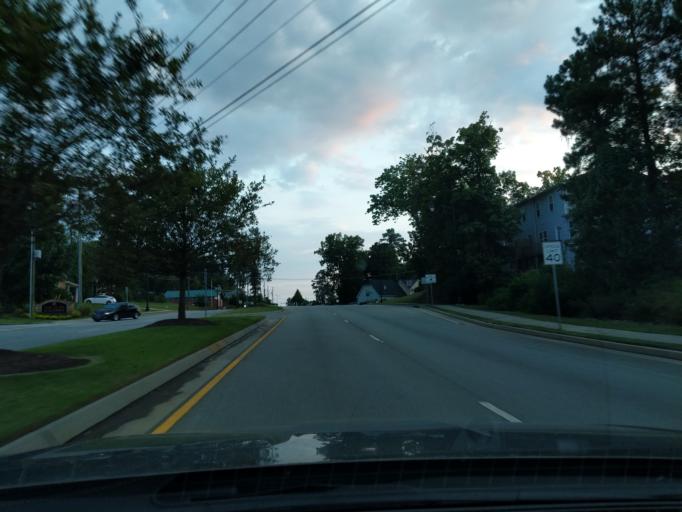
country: US
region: Georgia
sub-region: Columbia County
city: Martinez
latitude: 33.5159
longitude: -82.0254
